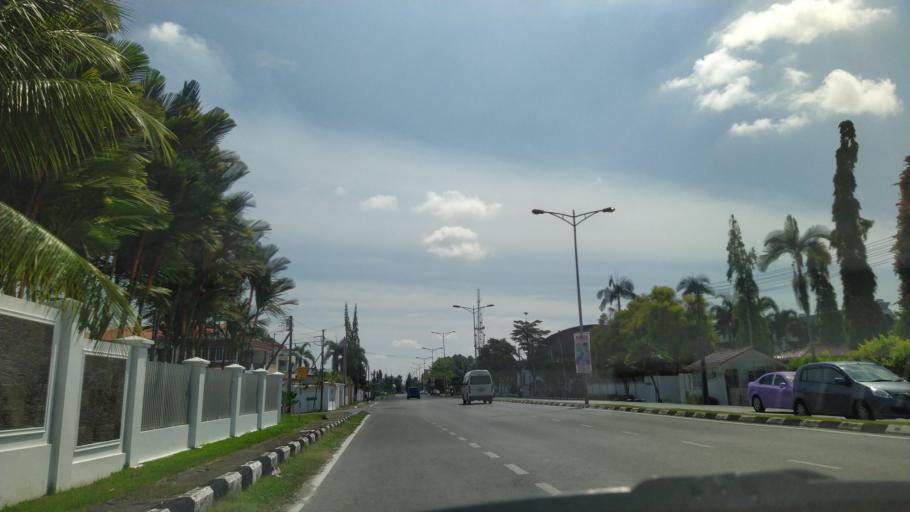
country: MY
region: Sarawak
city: Sibu
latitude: 2.3086
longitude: 111.8294
